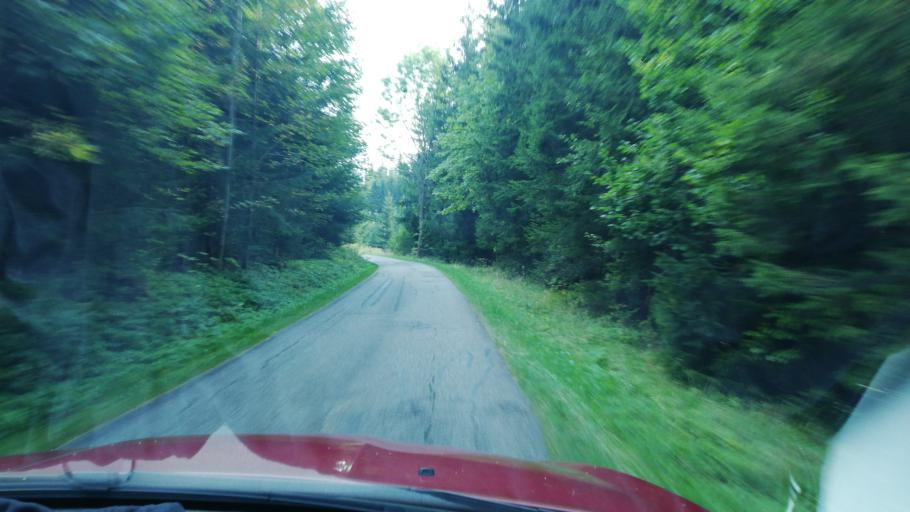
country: AT
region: Lower Austria
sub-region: Politischer Bezirk Zwettl
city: Langschlag
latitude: 48.4818
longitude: 14.8401
